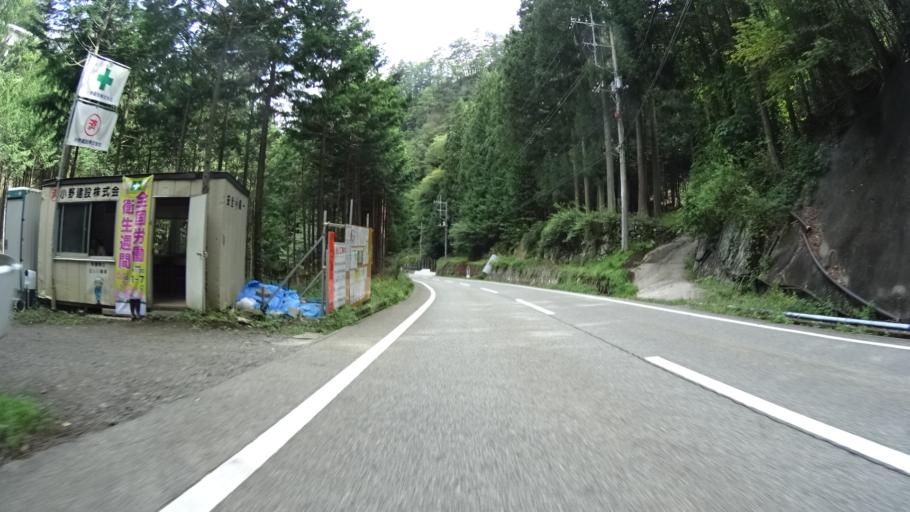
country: JP
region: Yamanashi
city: Kofu-shi
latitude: 35.7596
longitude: 138.5622
